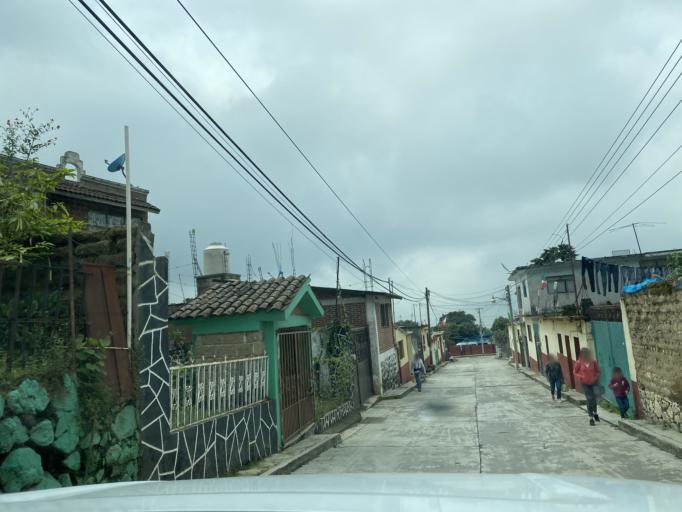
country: MX
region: Morelos
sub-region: Yecapixtla
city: Achichipico
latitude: 18.9468
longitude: -98.8250
